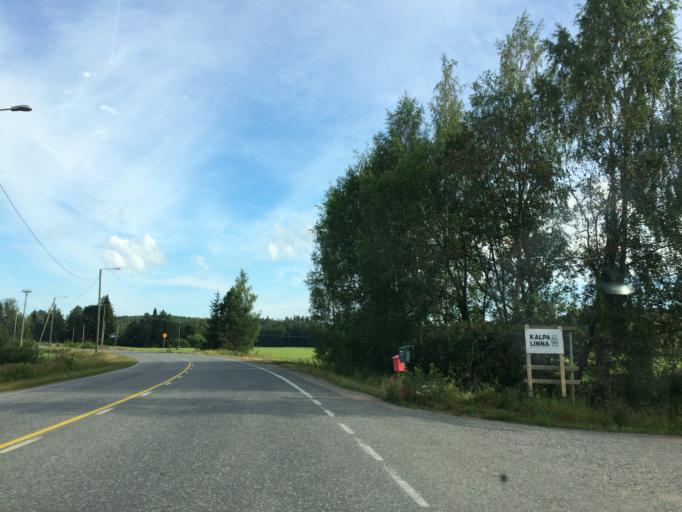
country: FI
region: Haeme
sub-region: Haemeenlinna
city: Janakkala
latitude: 60.9230
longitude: 24.5898
